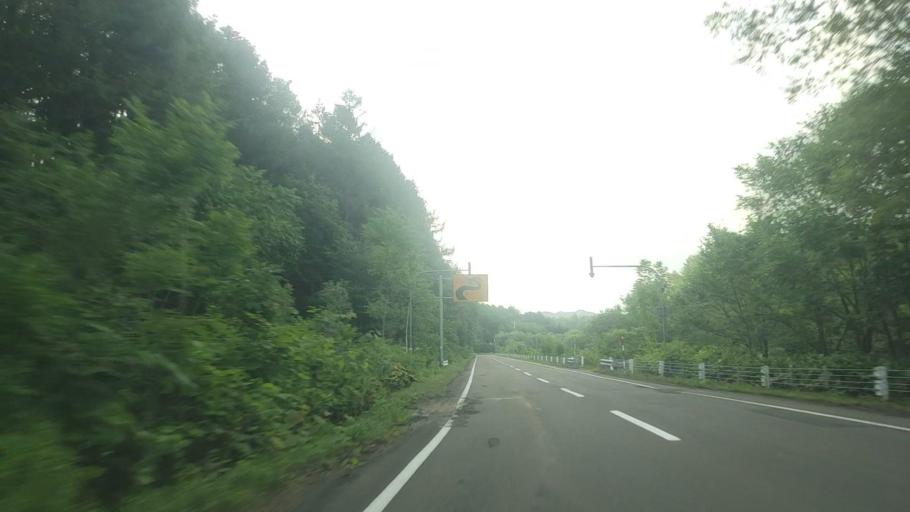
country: JP
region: Hokkaido
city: Bibai
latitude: 43.1225
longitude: 142.1037
